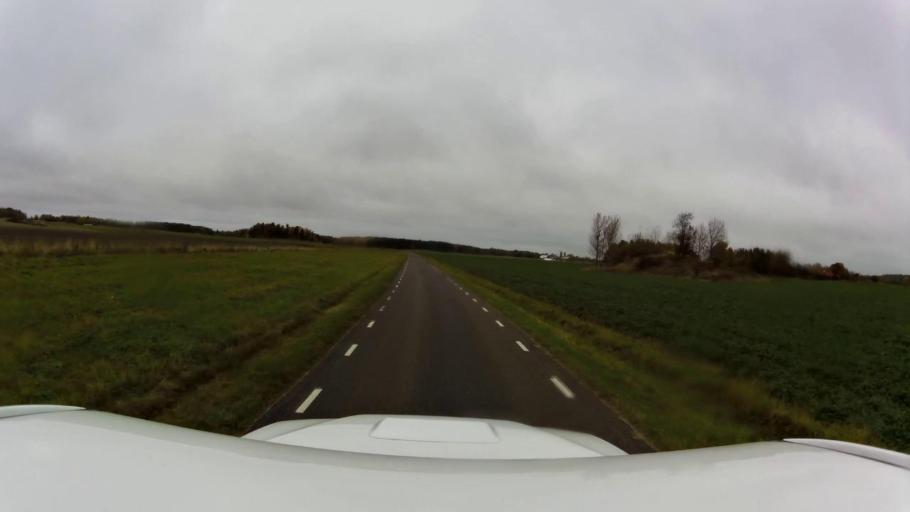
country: SE
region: OEstergoetland
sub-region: Linkopings Kommun
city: Linghem
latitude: 58.4828
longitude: 15.8153
